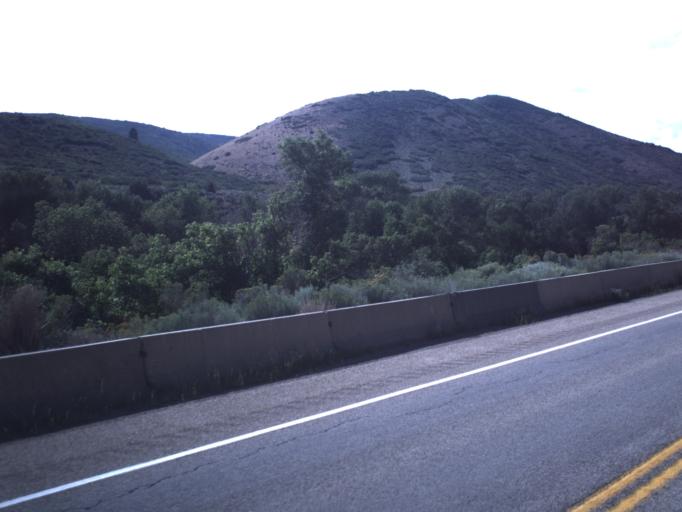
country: US
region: Utah
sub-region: Wasatch County
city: Heber
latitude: 40.4359
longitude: -111.3565
